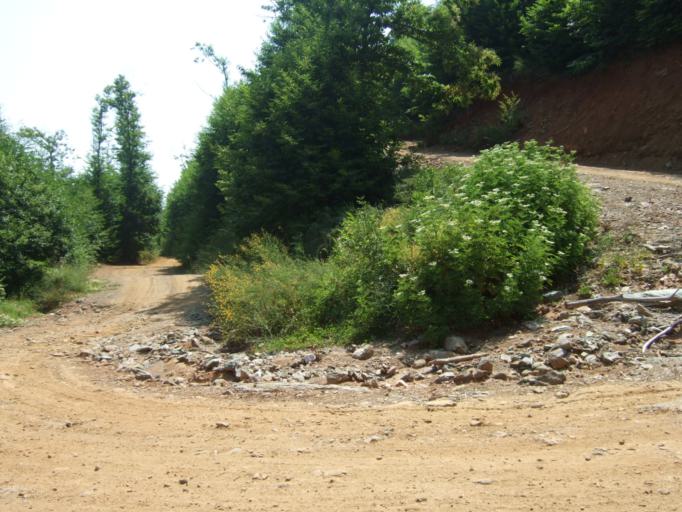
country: GR
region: Mount Athos
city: Karyes
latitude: 40.1876
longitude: 24.3017
